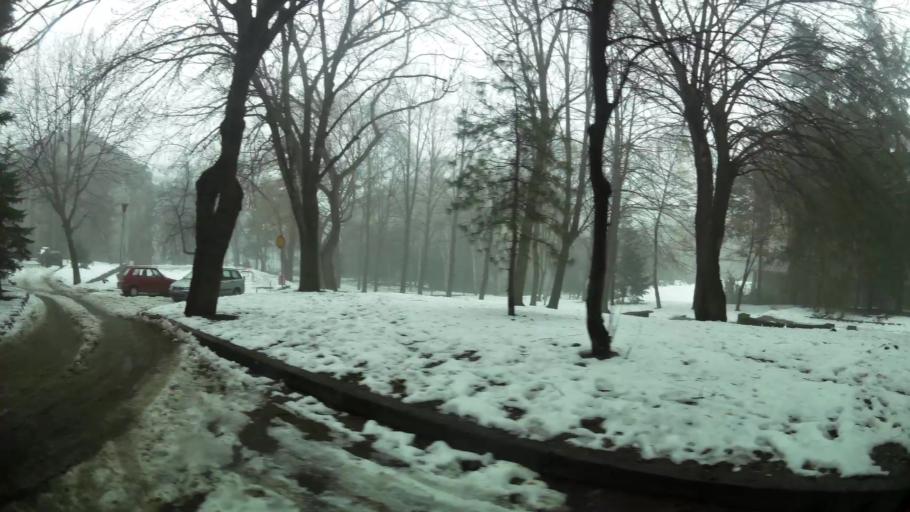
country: RS
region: Central Serbia
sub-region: Belgrade
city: Vozdovac
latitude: 44.7758
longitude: 20.4665
